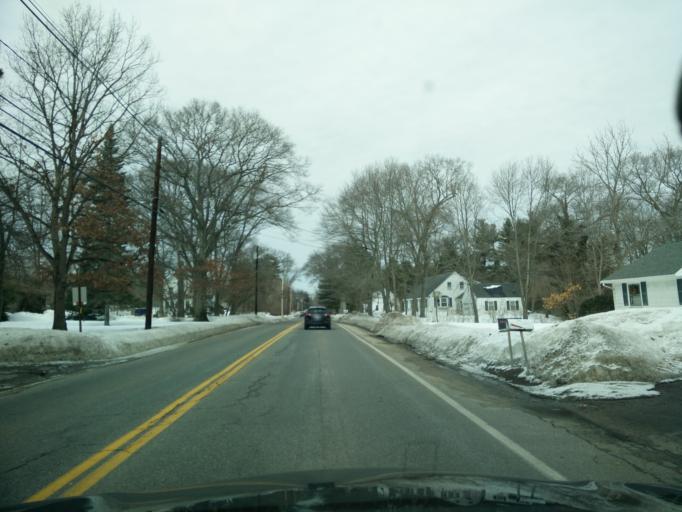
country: US
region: Massachusetts
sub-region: Norfolk County
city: Walpole
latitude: 42.1770
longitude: -71.2432
